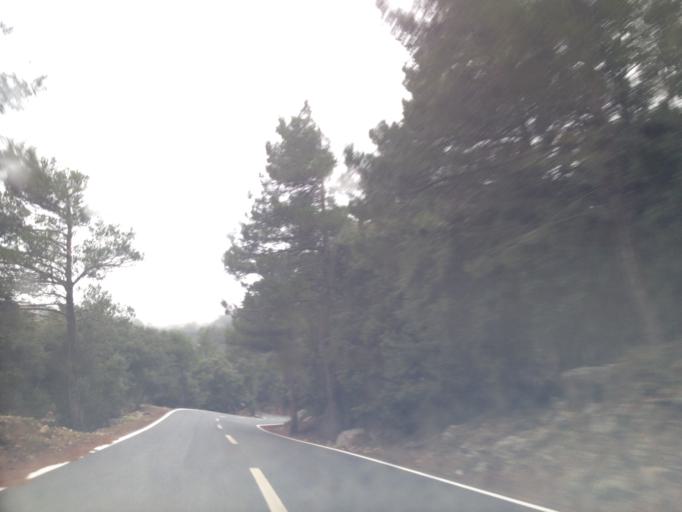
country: ES
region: Balearic Islands
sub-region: Illes Balears
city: Fornalutx
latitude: 39.7952
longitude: 2.7771
